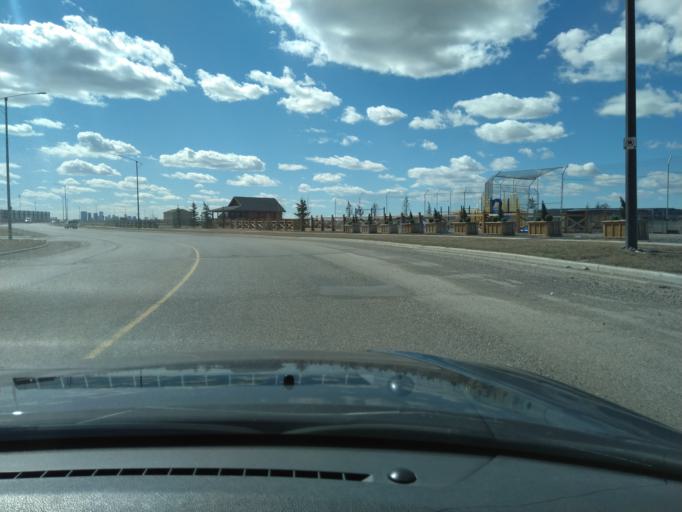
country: CA
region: Alberta
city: Calgary
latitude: 51.1360
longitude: -114.0361
